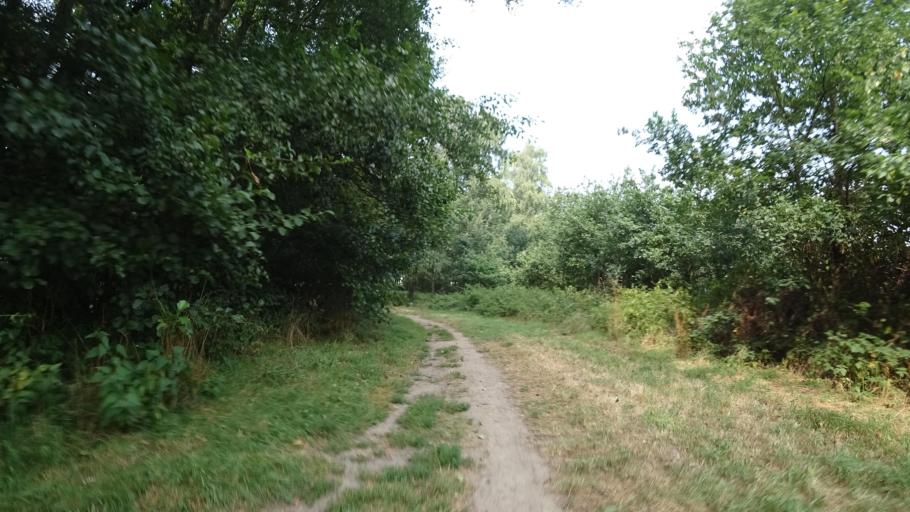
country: DE
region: North Rhine-Westphalia
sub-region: Regierungsbezirk Detmold
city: Guetersloh
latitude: 51.9229
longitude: 8.4380
